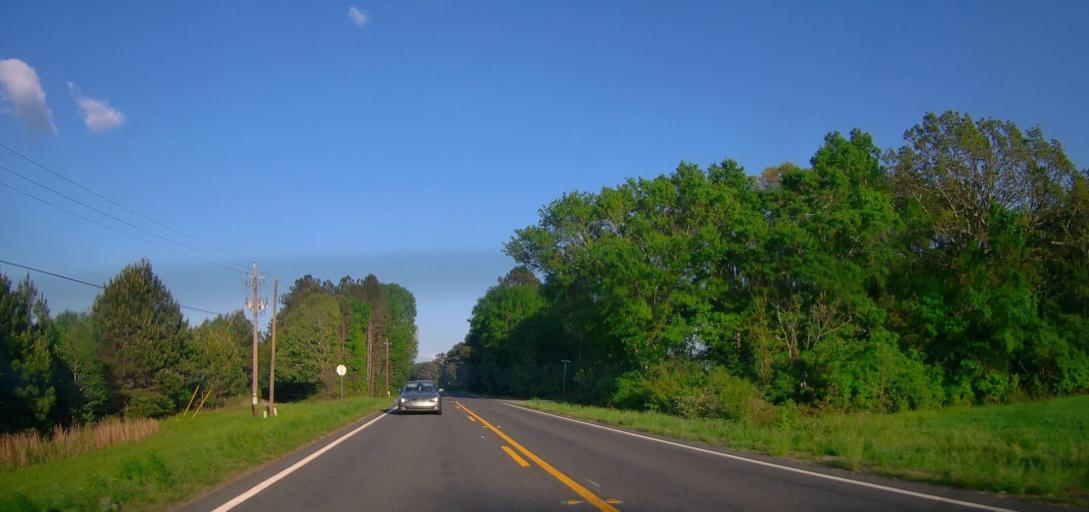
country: US
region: Georgia
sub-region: Walton County
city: Social Circle
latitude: 33.5111
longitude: -83.6843
